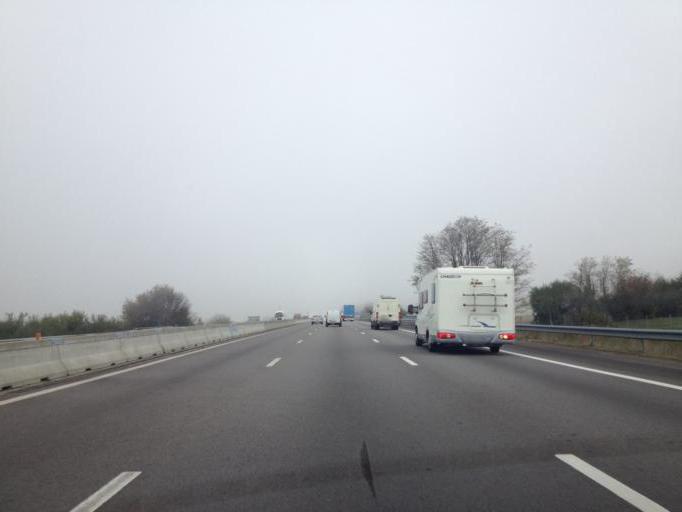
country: FR
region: Rhone-Alpes
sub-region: Departement de la Drome
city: Savasse
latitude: 44.6175
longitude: 4.7930
